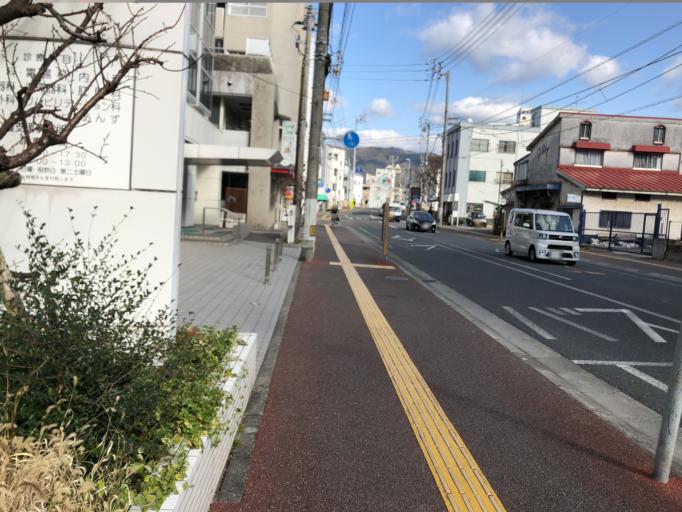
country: JP
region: Kochi
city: Kochi-shi
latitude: 33.5635
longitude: 133.5370
